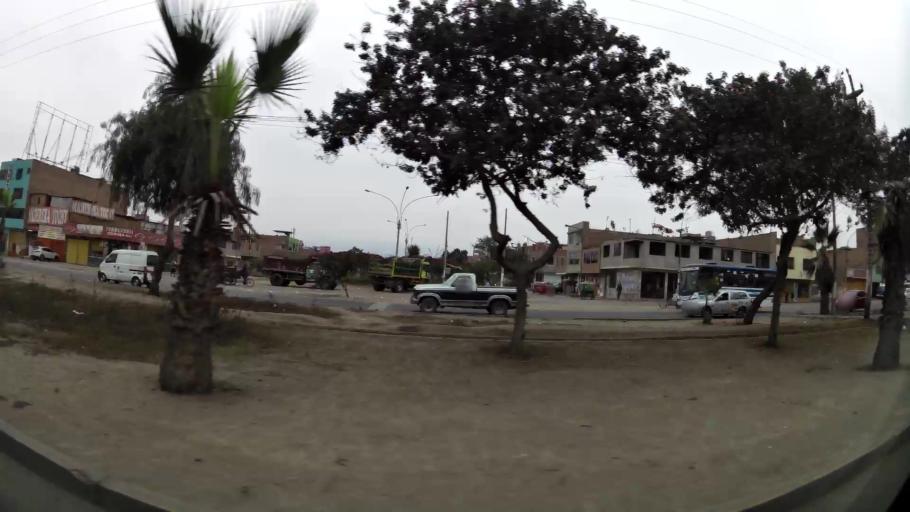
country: PE
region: Lima
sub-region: Lima
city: Urb. Santo Domingo
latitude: -11.9196
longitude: -77.0503
